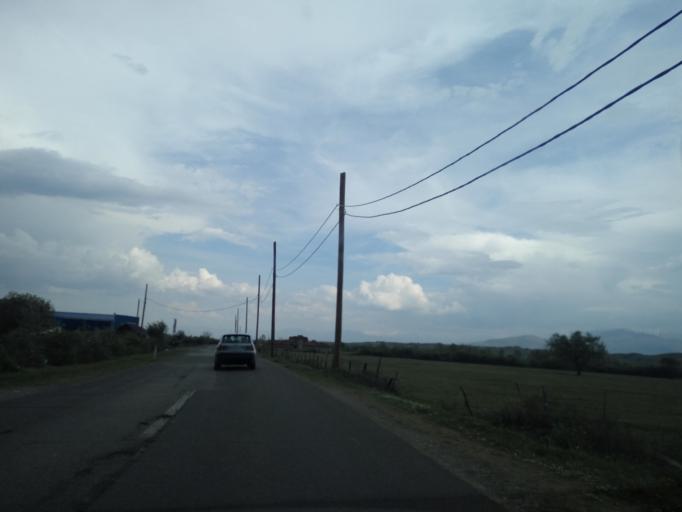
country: XK
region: Gjakova
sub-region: Komuna e Gjakoves
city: Gjakove
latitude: 42.3760
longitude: 20.3350
